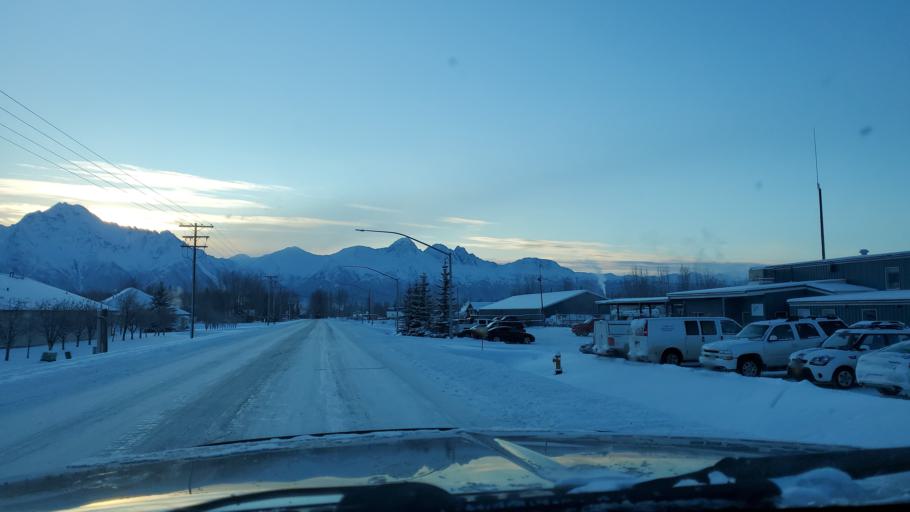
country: US
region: Alaska
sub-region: Matanuska-Susitna Borough
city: Palmer
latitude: 61.5886
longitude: -149.1106
